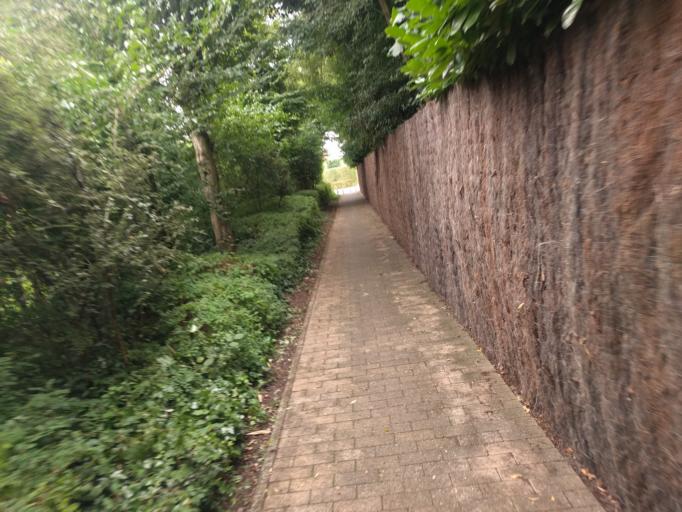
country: BE
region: Flanders
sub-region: Provincie West-Vlaanderen
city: Wevelgem
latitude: 50.8160
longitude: 3.1839
